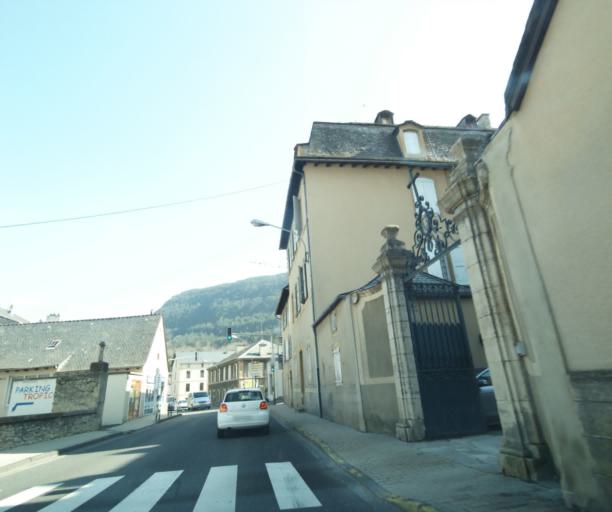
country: FR
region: Languedoc-Roussillon
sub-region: Departement de la Lozere
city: Mende
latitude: 44.5177
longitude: 3.5032
